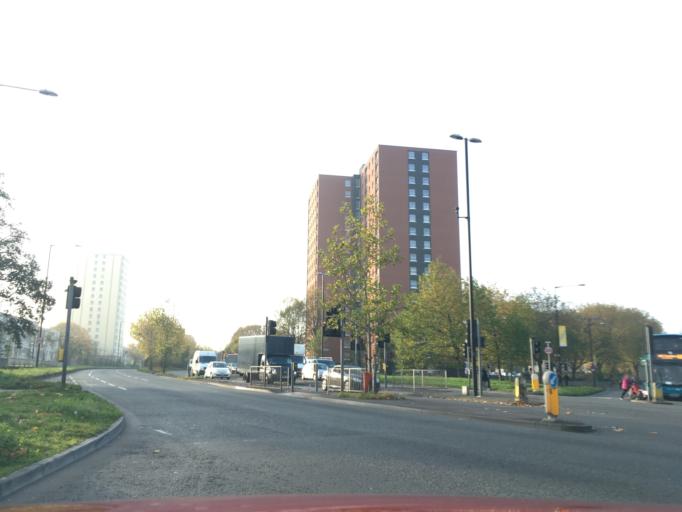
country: GB
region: England
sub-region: Bristol
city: Bristol
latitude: 51.4634
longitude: -2.5709
